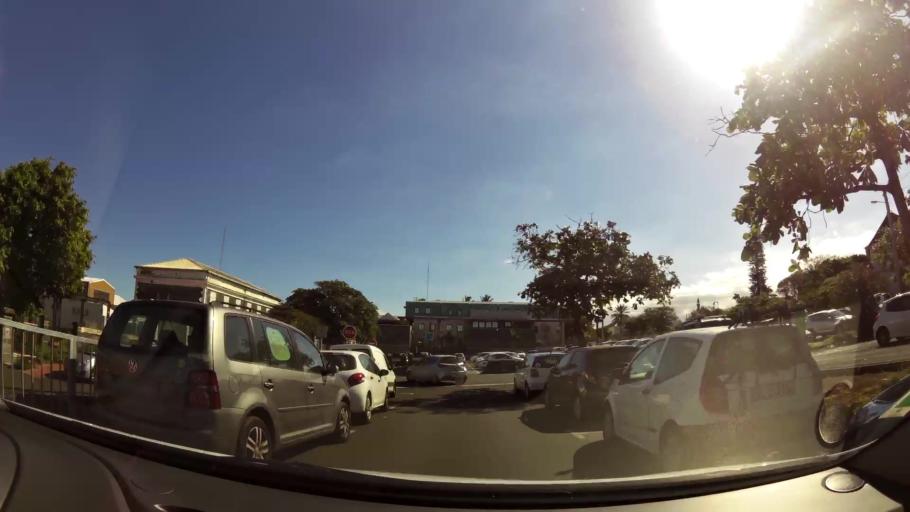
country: RE
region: Reunion
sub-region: Reunion
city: Saint-Pierre
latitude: -21.3427
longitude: 55.4780
